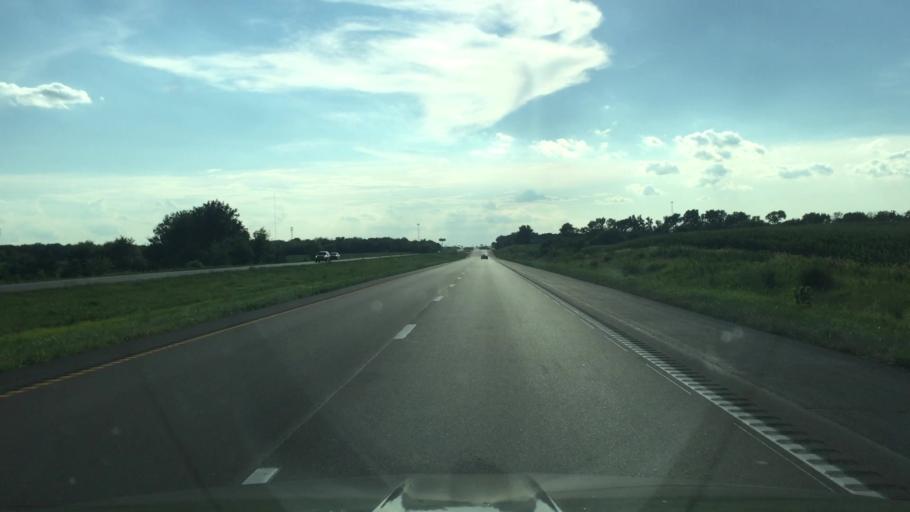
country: US
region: Missouri
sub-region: Pettis County
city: La Monte
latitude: 38.7625
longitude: -93.4018
